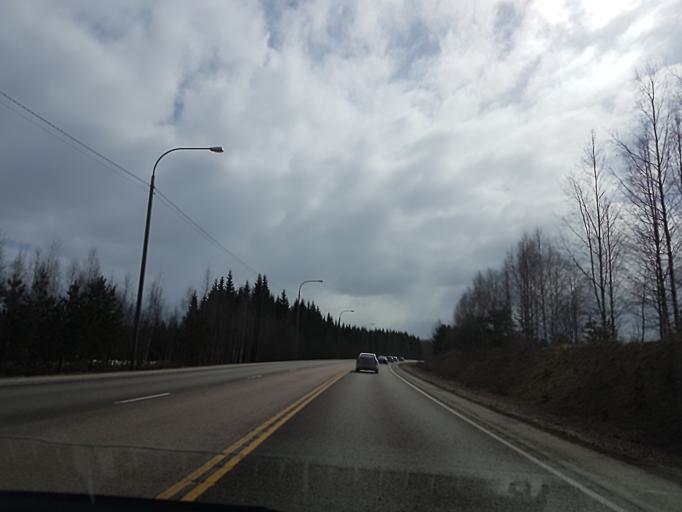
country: FI
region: Northern Savo
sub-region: Varkaus
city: Leppaevirta
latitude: 62.4629
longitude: 27.7842
